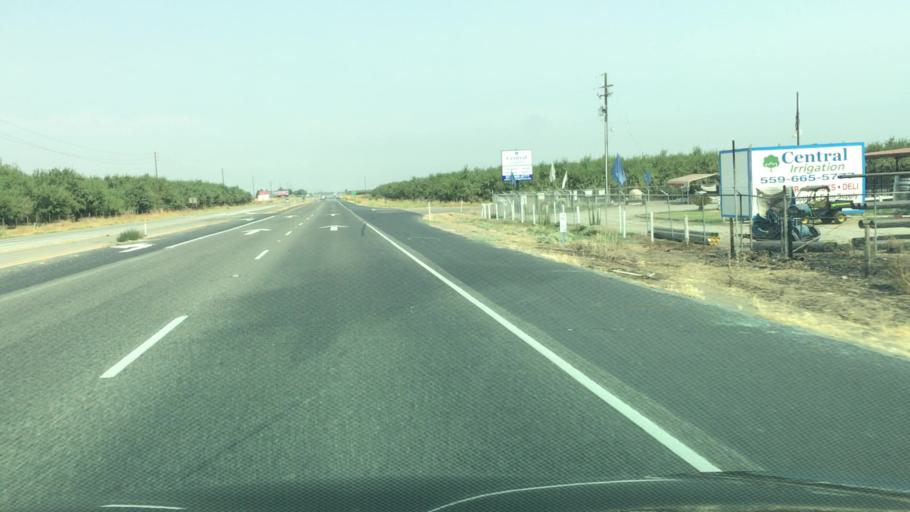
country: US
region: California
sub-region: Madera County
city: Chowchilla
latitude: 37.0836
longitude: -120.2669
